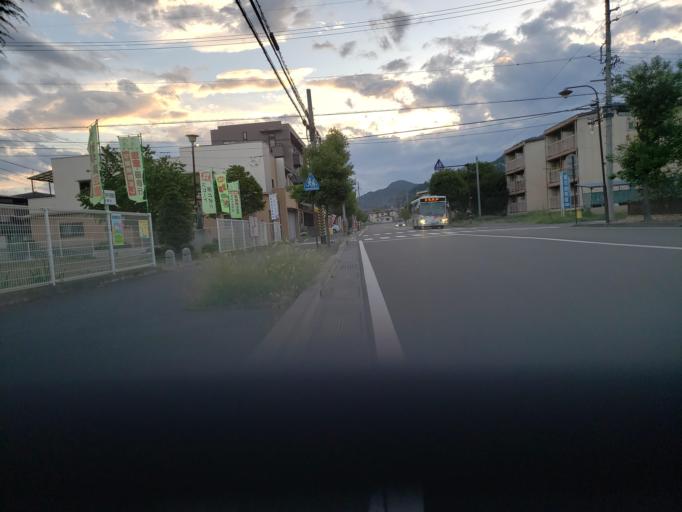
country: JP
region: Nagano
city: Nagano-shi
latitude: 36.6275
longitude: 138.1614
